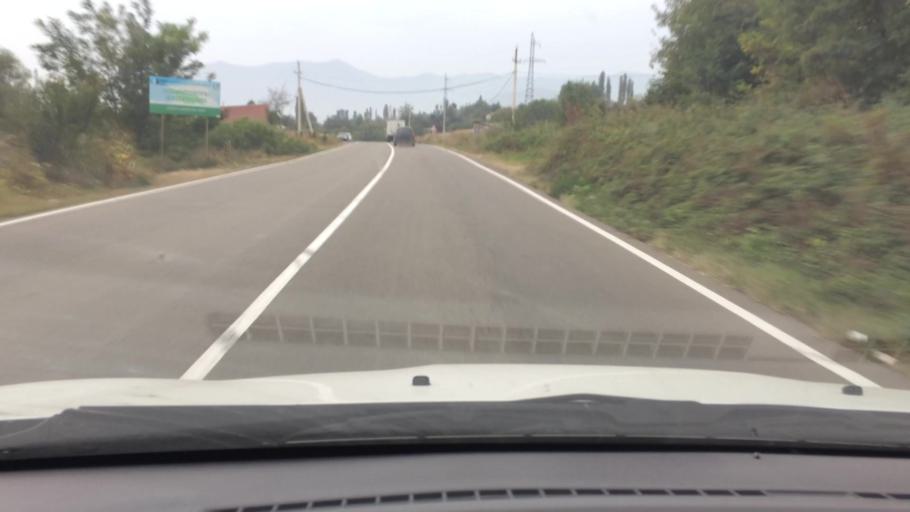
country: AM
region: Tavush
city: Bagratashen
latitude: 41.2687
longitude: 44.7910
